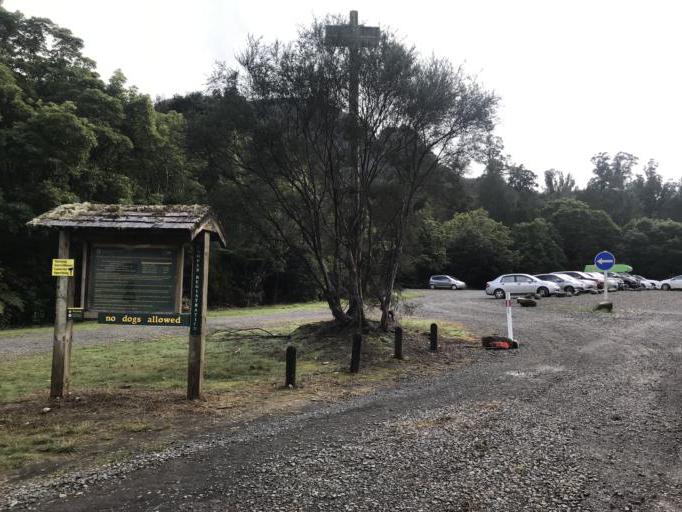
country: NZ
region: Waikato
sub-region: Thames-Coromandel District
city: Thames
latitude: -37.0665
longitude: 175.6676
